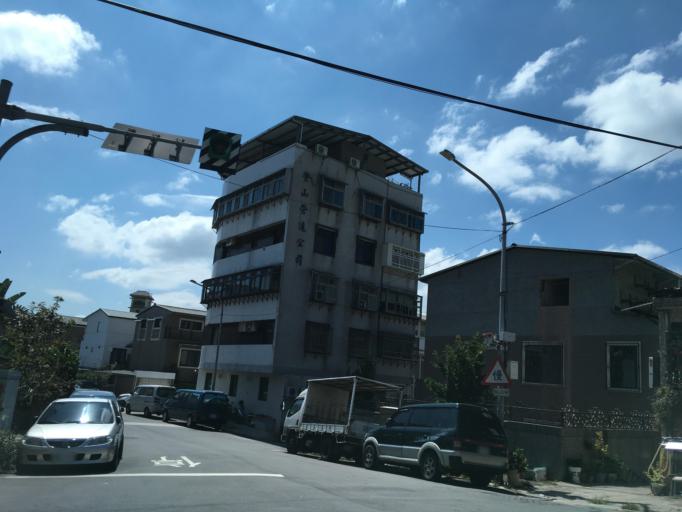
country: TW
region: Taipei
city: Taipei
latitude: 25.1443
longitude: 121.4977
